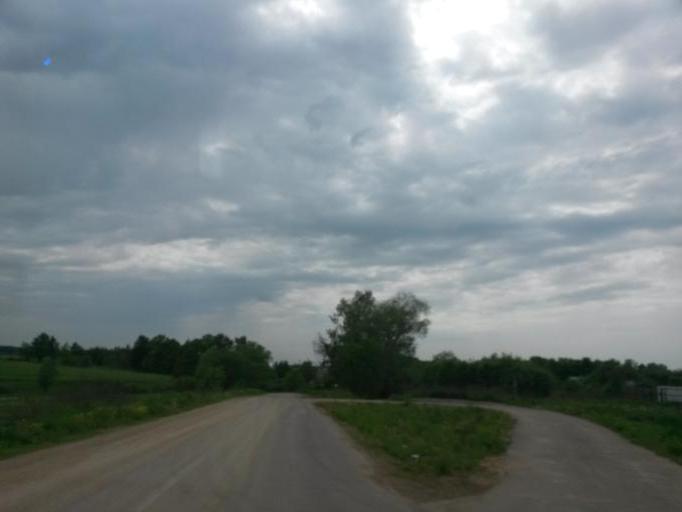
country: RU
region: Moskovskaya
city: Melikhovo
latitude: 55.1537
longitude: 37.6630
